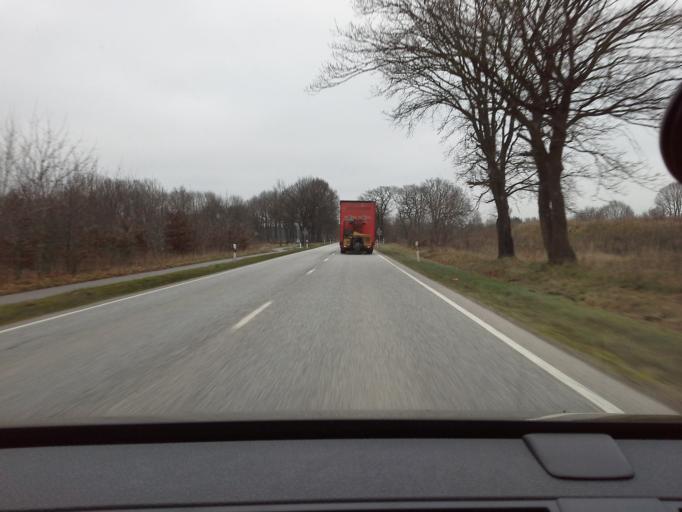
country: DE
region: Schleswig-Holstein
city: Lentfohrden
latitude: 53.8559
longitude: 9.8886
